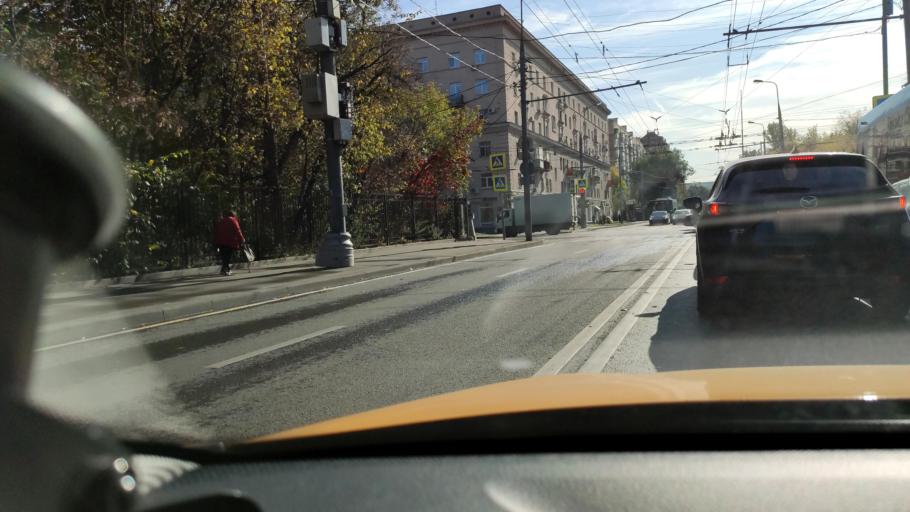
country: RU
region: Moskovskaya
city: Fili
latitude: 55.7478
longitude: 37.4943
